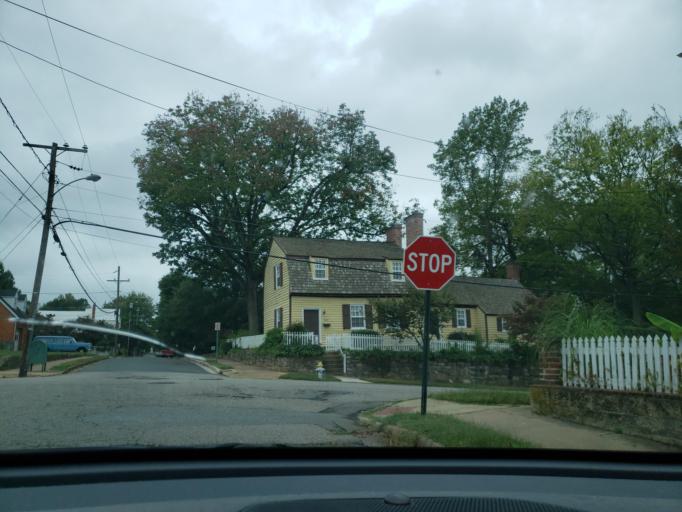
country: US
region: Virginia
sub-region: City of Fredericksburg
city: Fredericksburg
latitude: 38.3059
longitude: -77.4634
